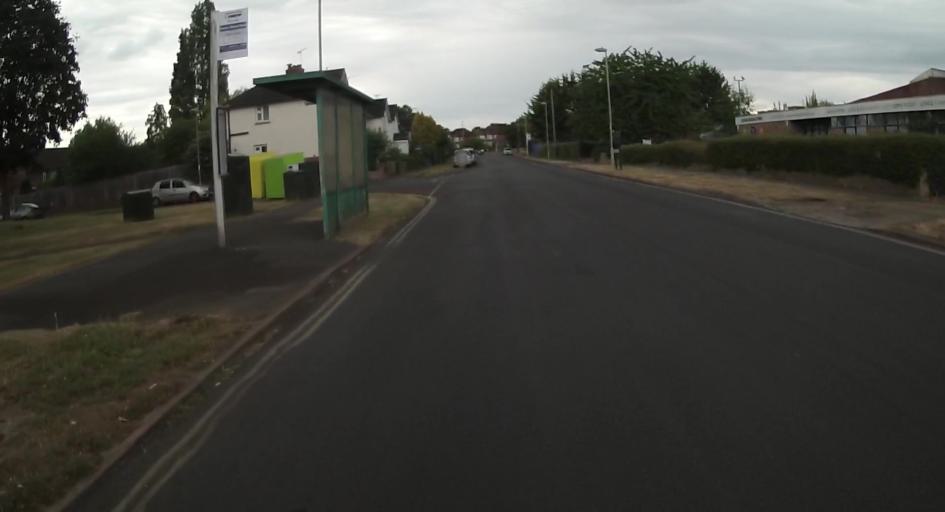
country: GB
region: England
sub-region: Hampshire
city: Aldershot
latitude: 51.2388
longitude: -0.7434
